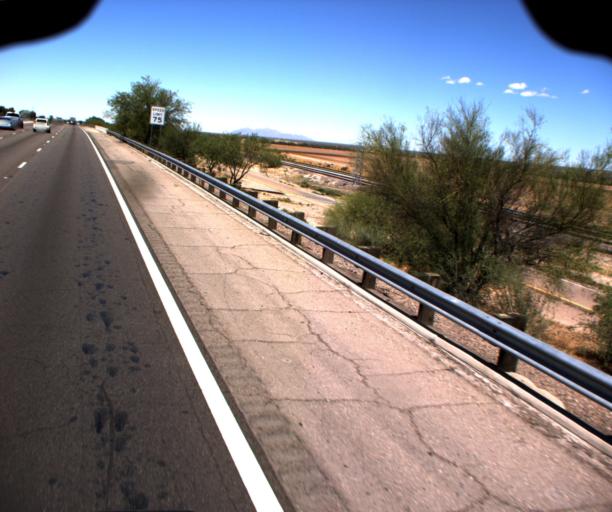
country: US
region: Arizona
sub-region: Pima County
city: Marana
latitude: 32.4081
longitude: -111.1407
